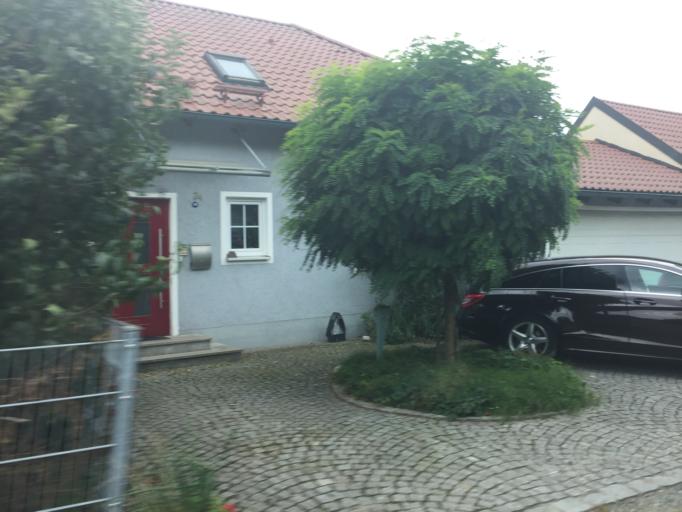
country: DE
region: Bavaria
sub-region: Upper Palatinate
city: Pressath
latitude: 49.7664
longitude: 11.9519
